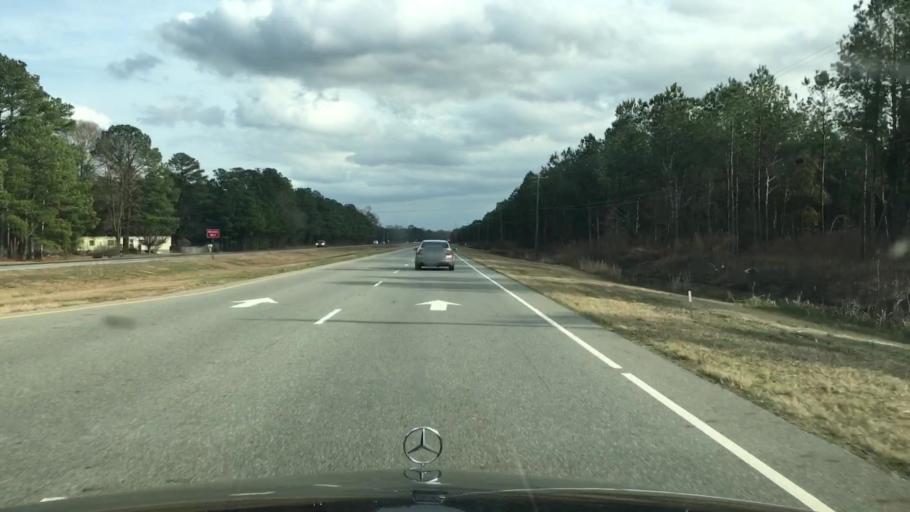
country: US
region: North Carolina
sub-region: Duplin County
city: Kenansville
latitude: 34.9508
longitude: -77.8922
